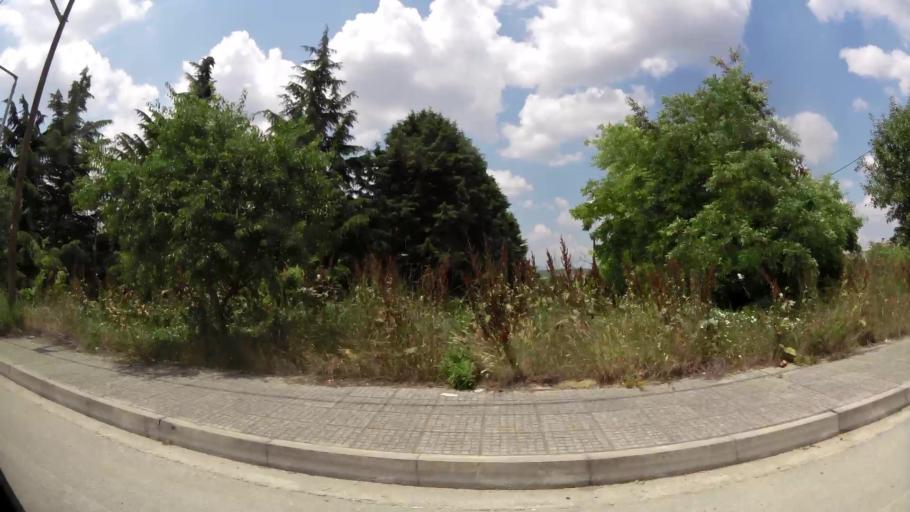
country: GR
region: West Macedonia
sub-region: Nomos Kozanis
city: Kozani
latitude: 40.2884
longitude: 21.7981
